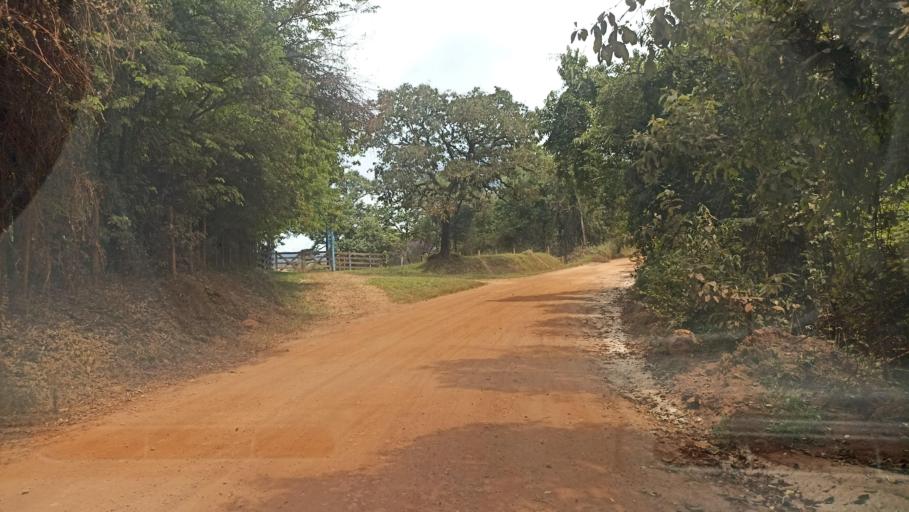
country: BR
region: Minas Gerais
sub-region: Itabirito
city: Itabirito
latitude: -20.3453
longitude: -43.7456
